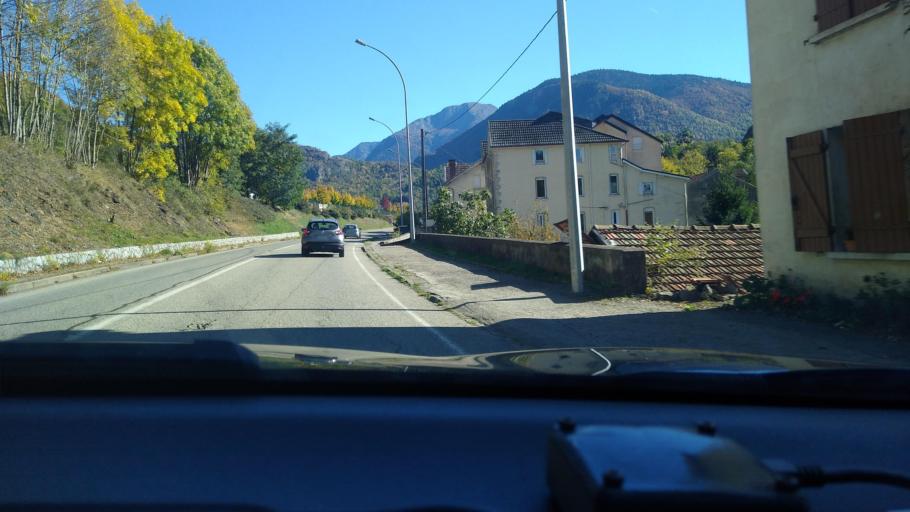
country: FR
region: Midi-Pyrenees
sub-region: Departement de l'Ariege
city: Ax-les-Thermes
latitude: 42.7272
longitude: 1.8293
